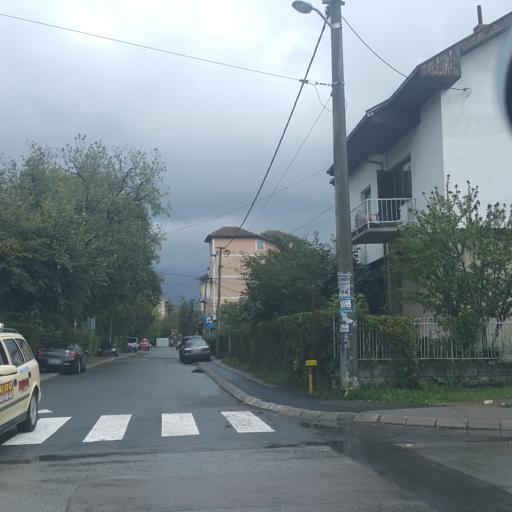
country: RS
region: Central Serbia
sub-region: Rasinski Okrug
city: Krusevac
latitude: 43.5745
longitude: 21.3397
